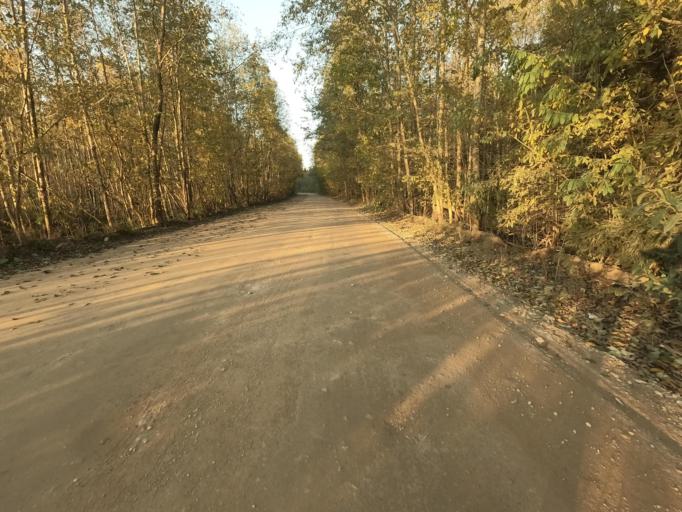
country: RU
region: Leningrad
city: Lyuban'
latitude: 58.9915
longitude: 31.1047
